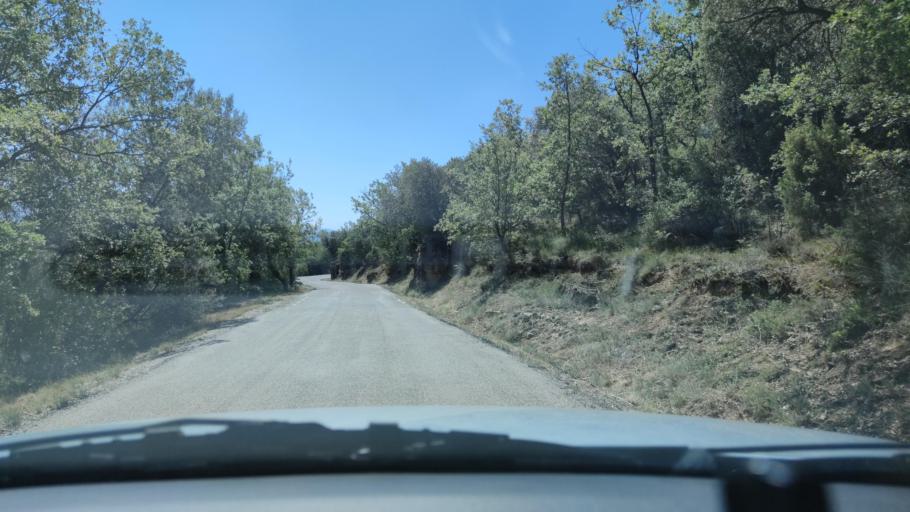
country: ES
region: Catalonia
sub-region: Provincia de Lleida
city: Tora de Riubregos
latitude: 41.8752
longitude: 1.4356
